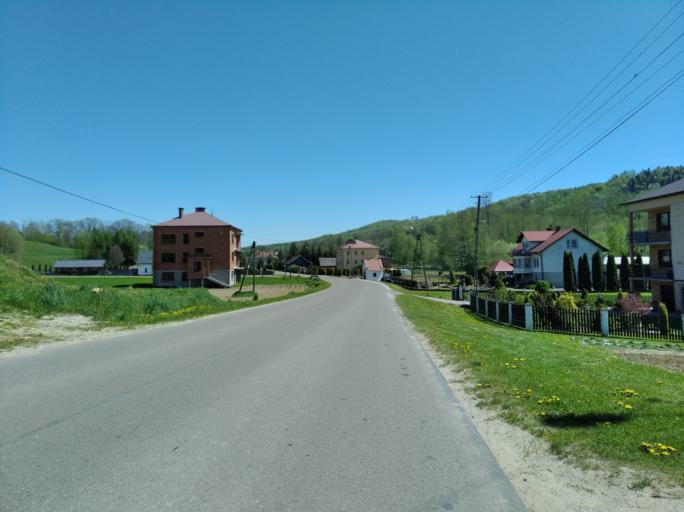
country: PL
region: Subcarpathian Voivodeship
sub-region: Powiat debicki
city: Brzostek
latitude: 49.9151
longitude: 21.4106
